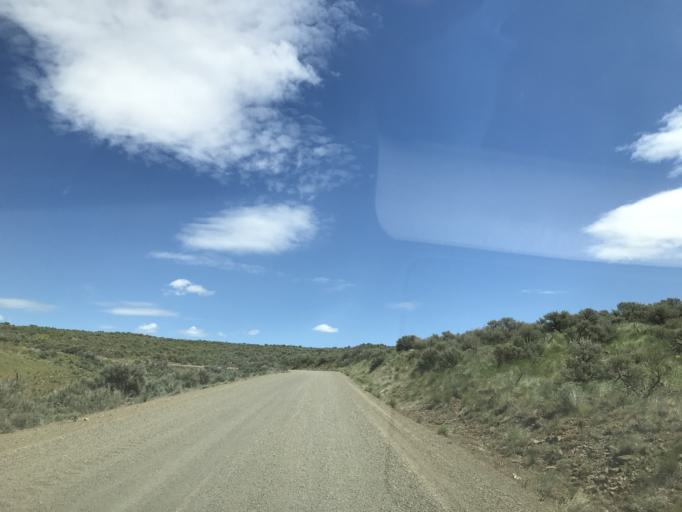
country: US
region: Washington
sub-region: Grant County
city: Quincy
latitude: 47.3128
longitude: -119.8214
